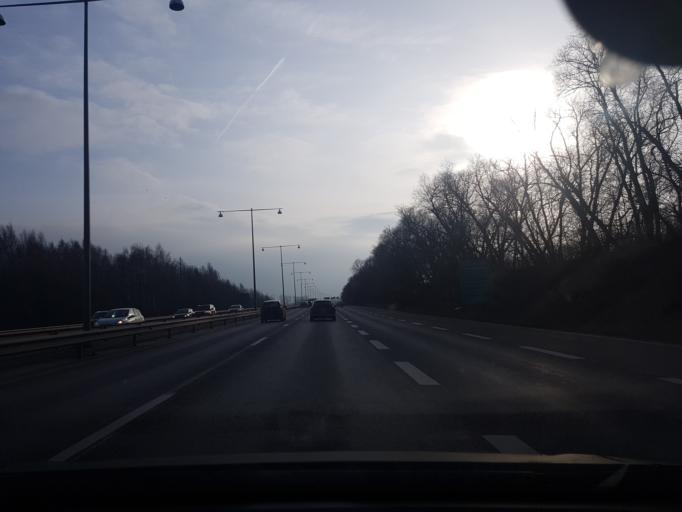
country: SE
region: Vaestra Goetaland
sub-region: Goteborg
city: Goeteborg
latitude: 57.7386
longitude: 11.9868
